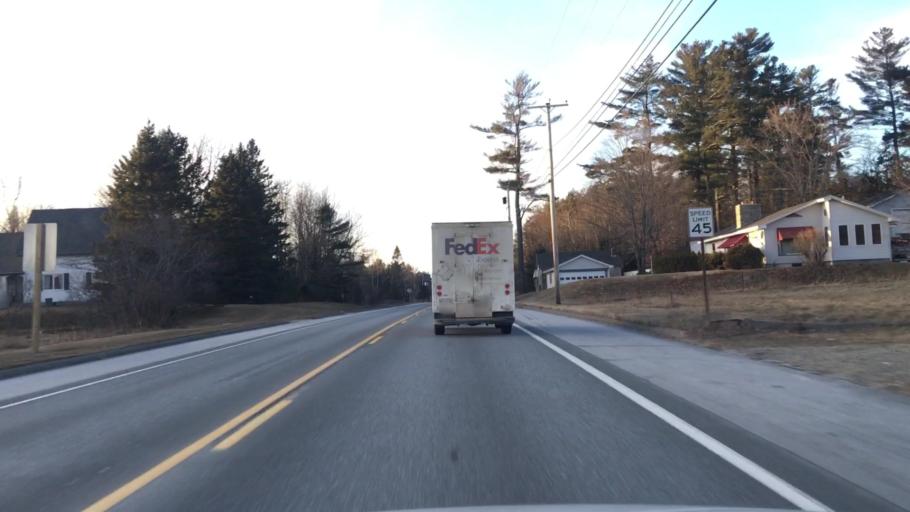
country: US
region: Maine
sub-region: Penobscot County
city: Holden
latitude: 44.7413
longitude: -68.6338
